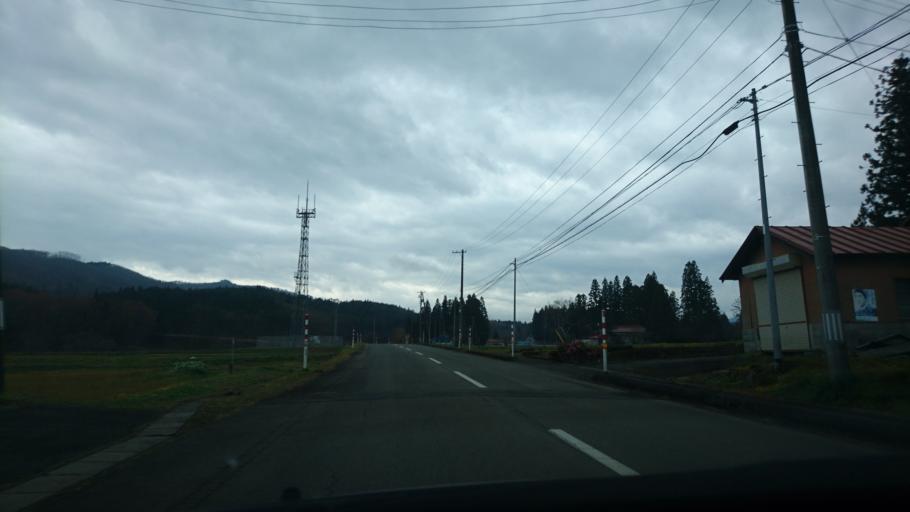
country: JP
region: Iwate
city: Ichinoseki
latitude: 38.9581
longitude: 140.9402
